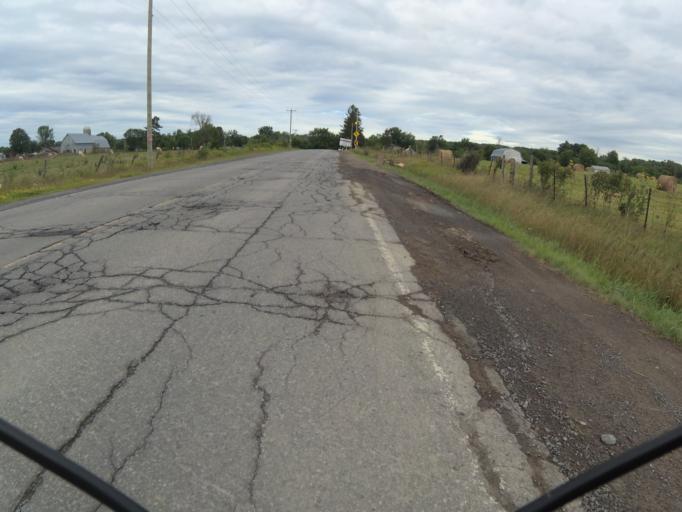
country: CA
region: Ontario
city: Bourget
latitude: 45.3897
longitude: -75.2781
